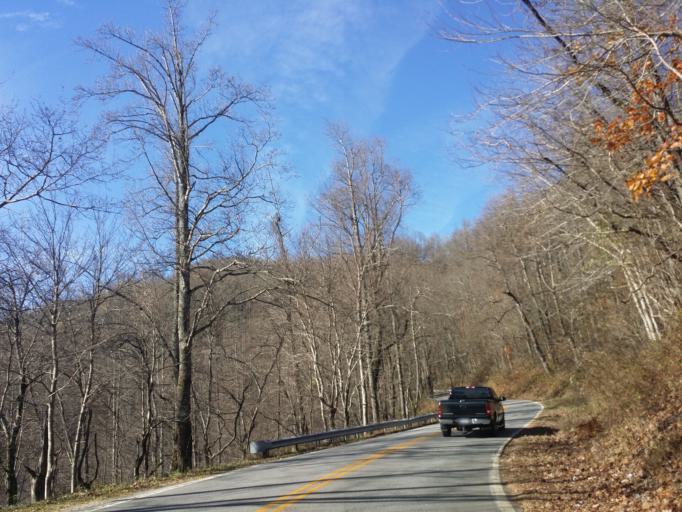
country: US
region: North Carolina
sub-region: McDowell County
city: Marion
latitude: 35.7670
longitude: -82.1635
